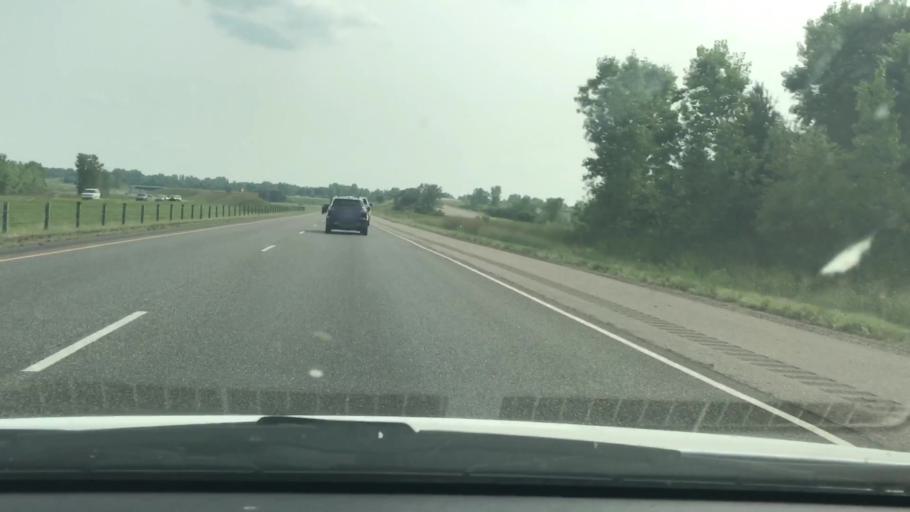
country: US
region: Minnesota
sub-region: Dakota County
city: Inver Grove Heights
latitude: 44.8326
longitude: -93.0598
